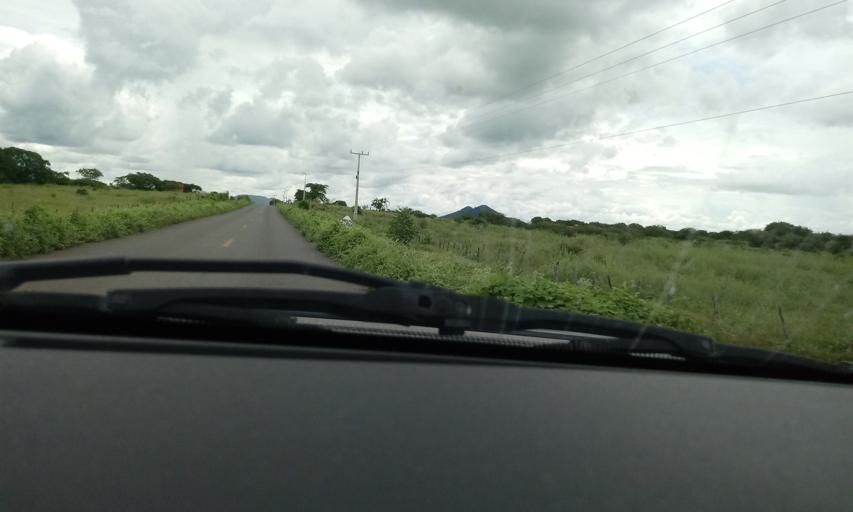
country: BR
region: Bahia
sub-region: Guanambi
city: Guanambi
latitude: -14.1071
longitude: -42.8671
